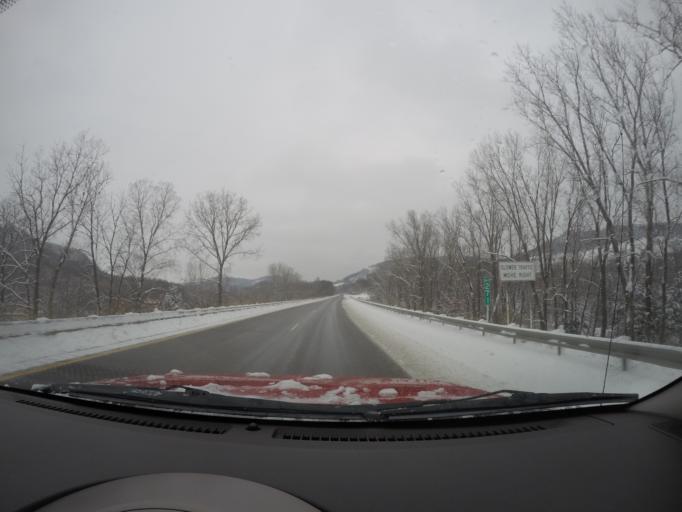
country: US
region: Wisconsin
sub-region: La Crosse County
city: Brice Prairie
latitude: 43.9177
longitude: -91.3686
